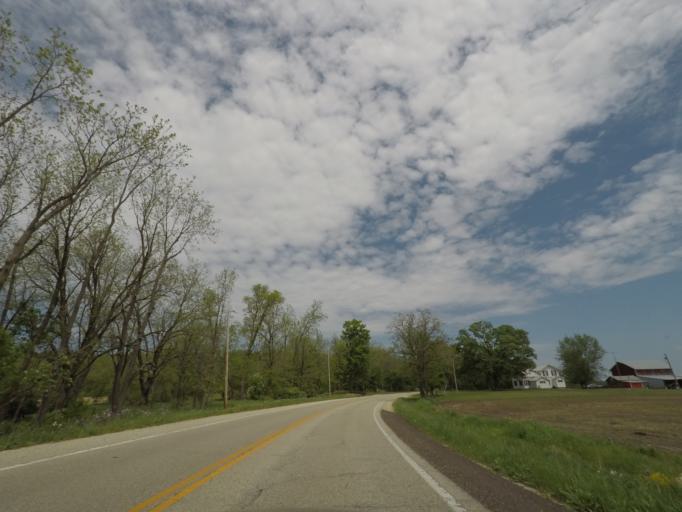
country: US
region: Wisconsin
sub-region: Rock County
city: Evansville
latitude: 42.7251
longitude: -89.2888
